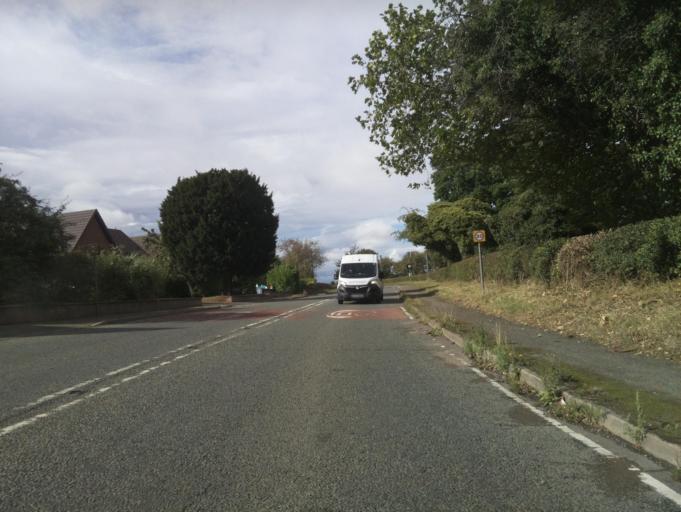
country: GB
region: England
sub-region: Telford and Wrekin
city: Madeley
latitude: 52.6010
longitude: -2.4034
